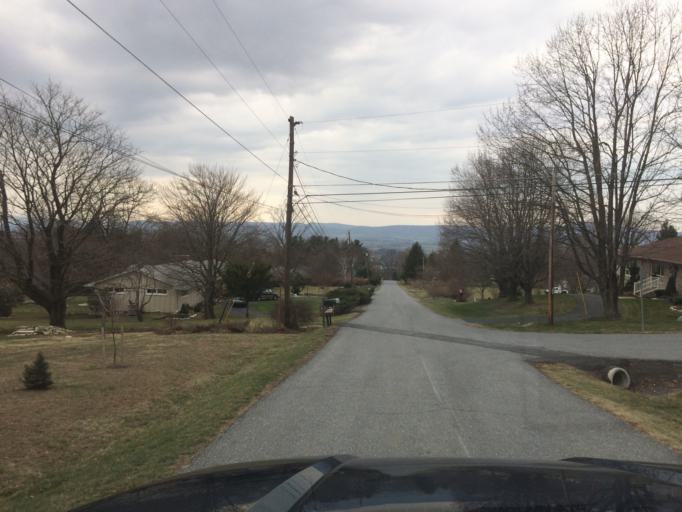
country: US
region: Maryland
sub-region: Frederick County
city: Braddock Heights
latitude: 39.4345
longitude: -77.4972
